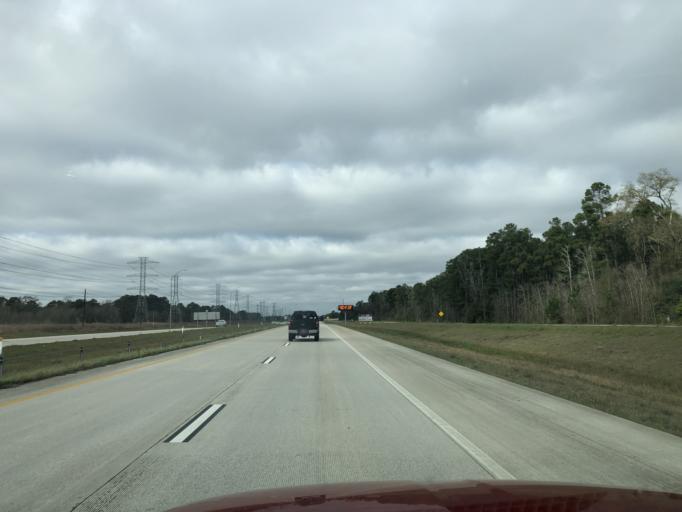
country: US
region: Texas
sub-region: Harris County
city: Spring
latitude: 30.0899
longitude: -95.4613
